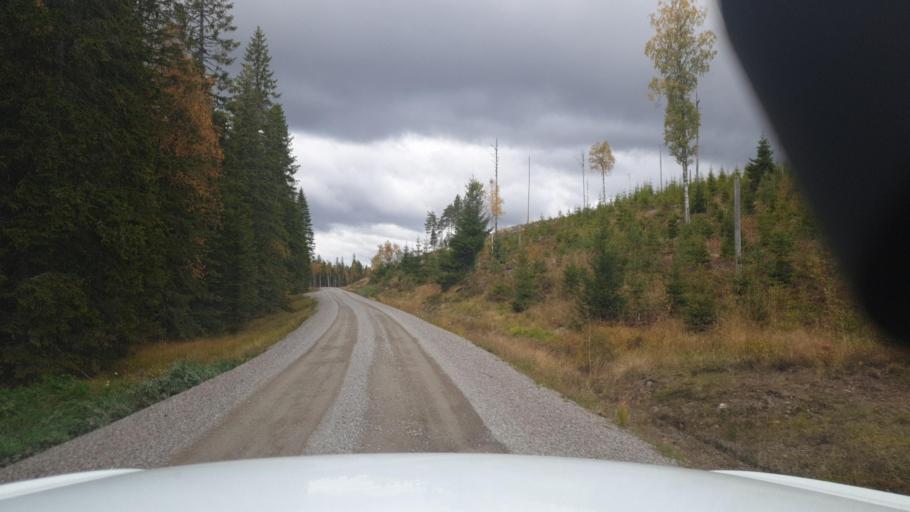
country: SE
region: Vaermland
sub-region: Eda Kommun
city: Charlottenberg
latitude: 60.0717
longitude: 12.6218
